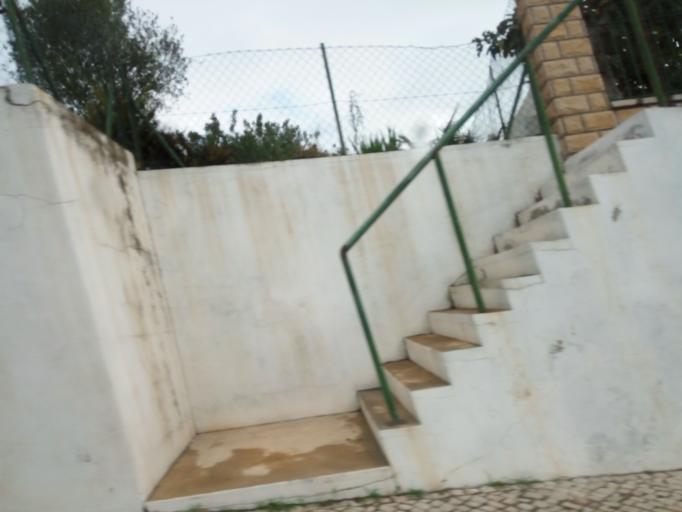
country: PT
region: Faro
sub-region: Loule
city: Loule
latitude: 37.1213
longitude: -8.0136
